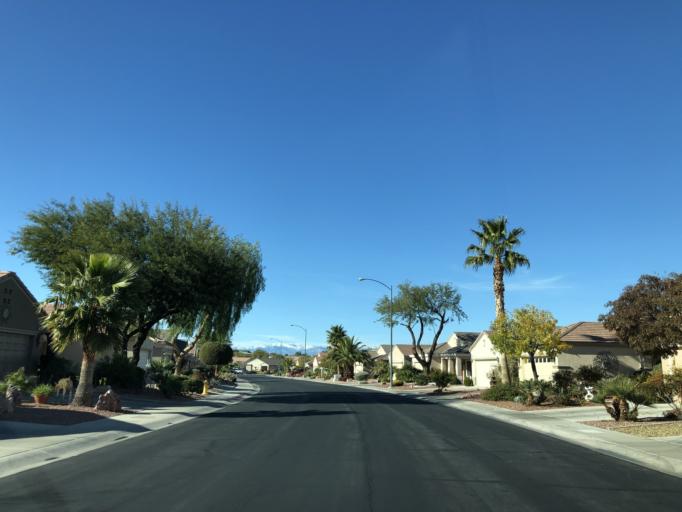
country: US
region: Nevada
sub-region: Clark County
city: Whitney
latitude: 36.0038
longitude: -115.0686
